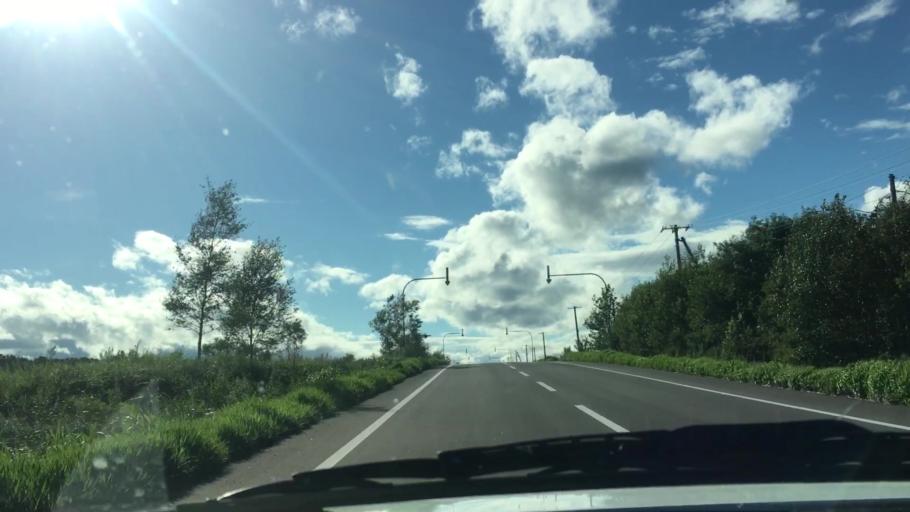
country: JP
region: Hokkaido
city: Otofuke
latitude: 43.1643
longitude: 143.1434
